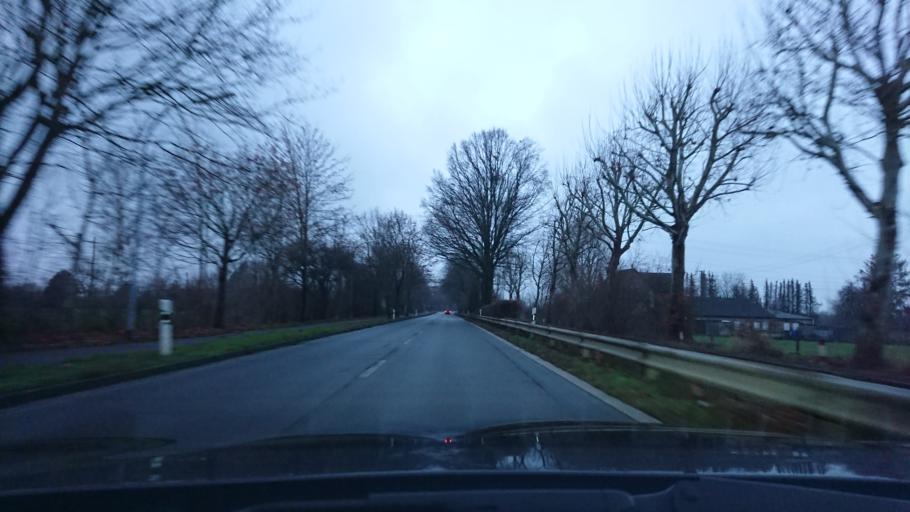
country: DE
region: North Rhine-Westphalia
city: Niederkassel
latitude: 50.8001
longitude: 7.0458
